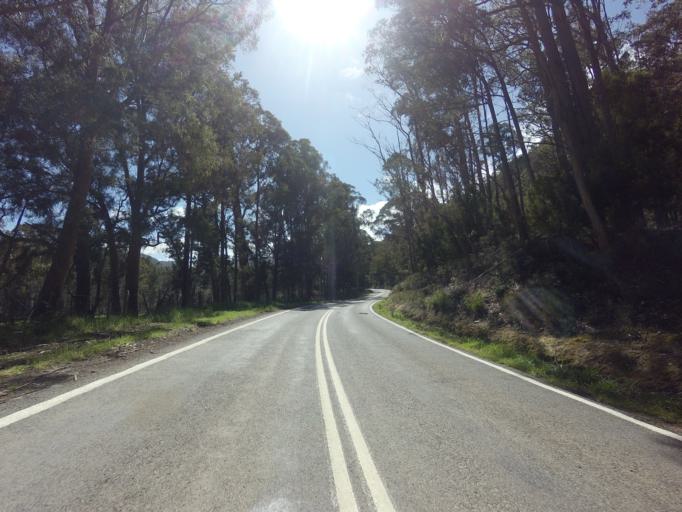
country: AU
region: Tasmania
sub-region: Derwent Valley
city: New Norfolk
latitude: -42.6945
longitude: 146.7138
